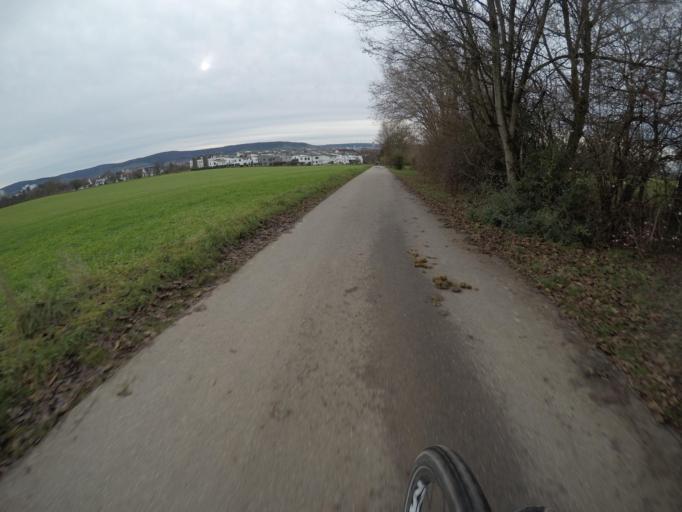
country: DE
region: Baden-Wuerttemberg
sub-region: Regierungsbezirk Stuttgart
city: Waiblingen
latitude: 48.8435
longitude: 9.3295
